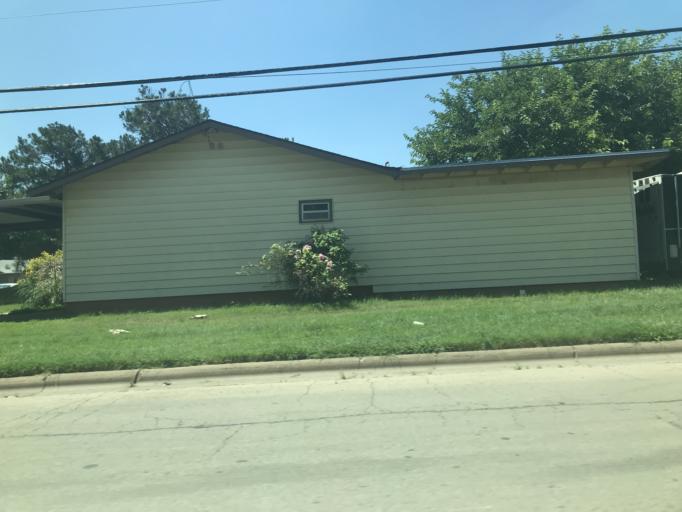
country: US
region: Texas
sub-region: Taylor County
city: Abilene
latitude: 32.4632
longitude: -99.7547
